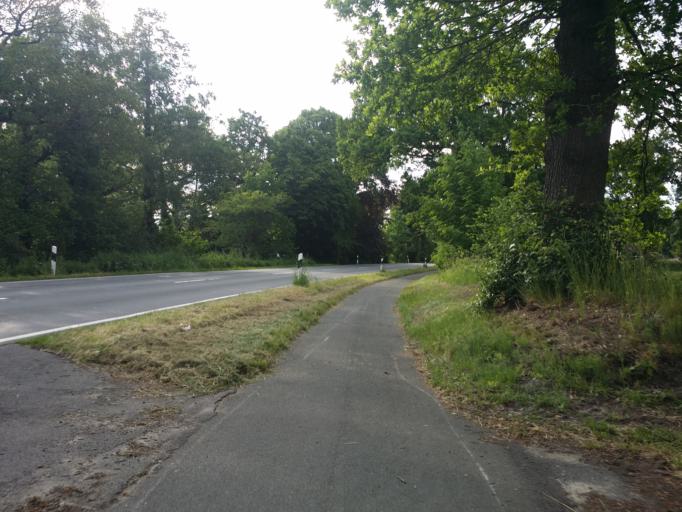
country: DE
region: Lower Saxony
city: Wittmund
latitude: 53.5235
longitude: 7.7840
